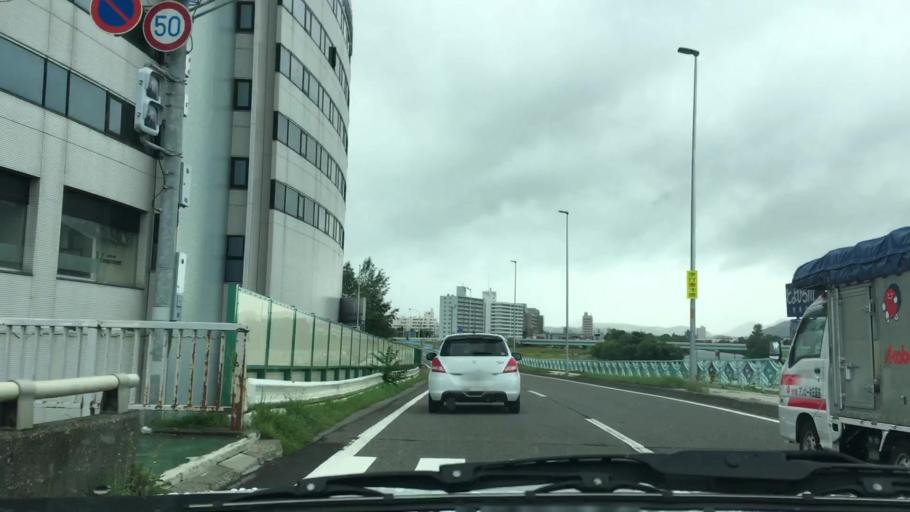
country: JP
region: Hokkaido
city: Sapporo
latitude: 43.0348
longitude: 141.3570
